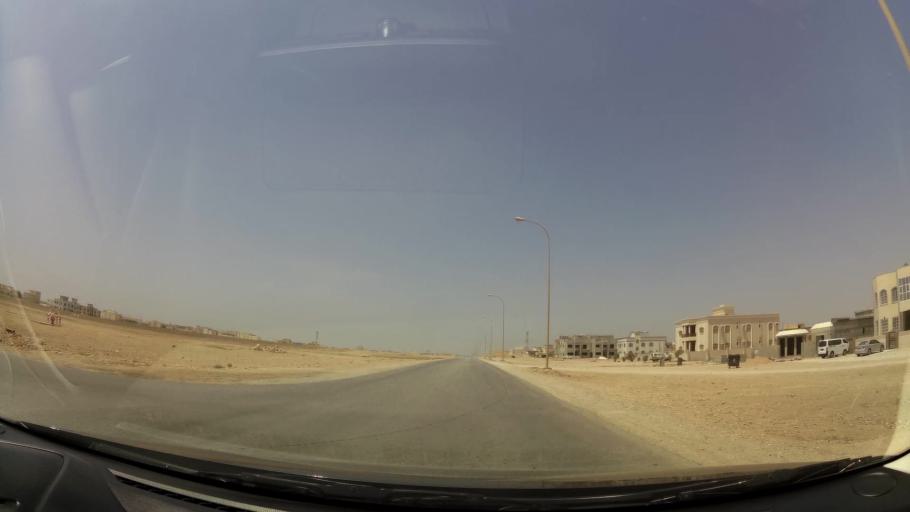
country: OM
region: Zufar
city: Salalah
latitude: 17.0865
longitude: 54.2053
